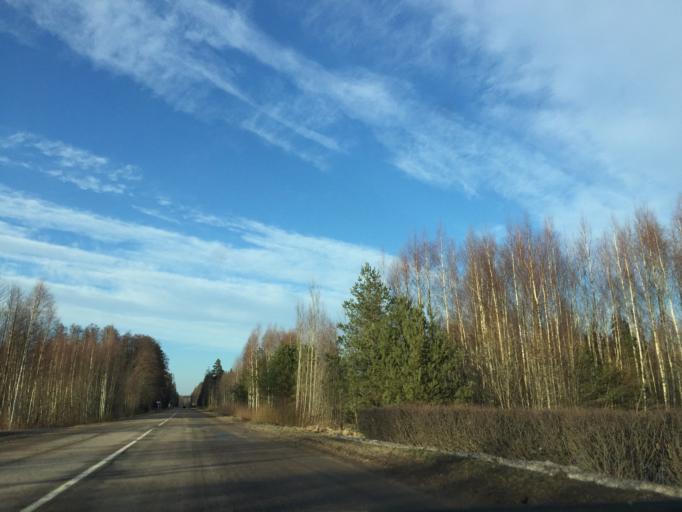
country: LV
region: Kekava
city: Balozi
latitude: 56.7373
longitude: 24.1090
